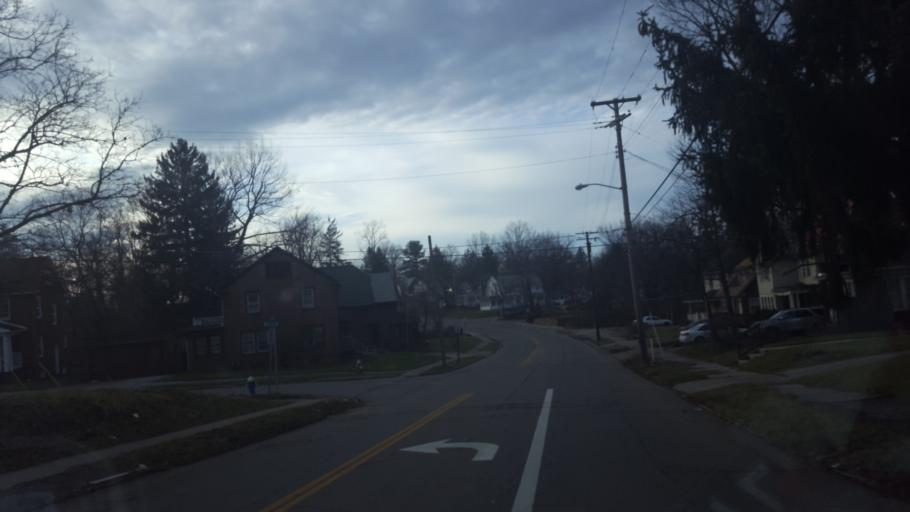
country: US
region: Ohio
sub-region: Richland County
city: Mansfield
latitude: 40.7645
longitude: -82.5375
